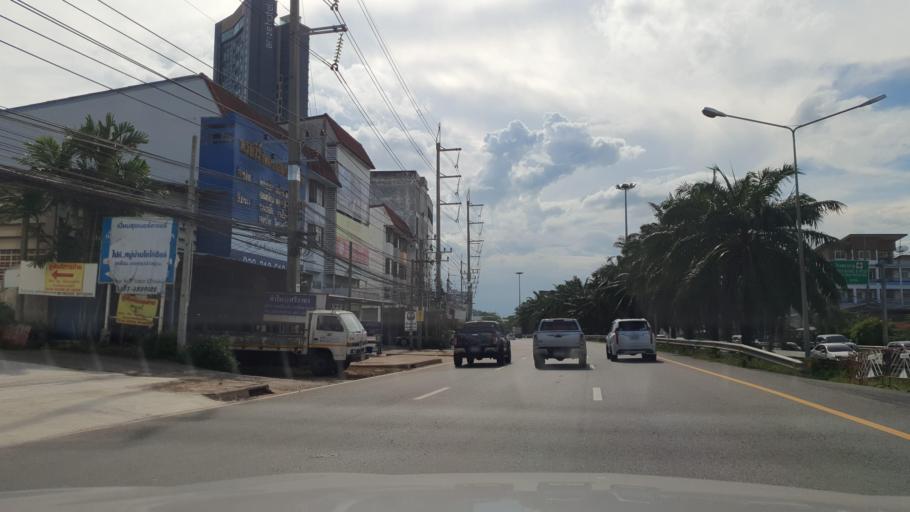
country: TH
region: Chon Buri
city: Si Racha
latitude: 13.1583
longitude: 100.9218
